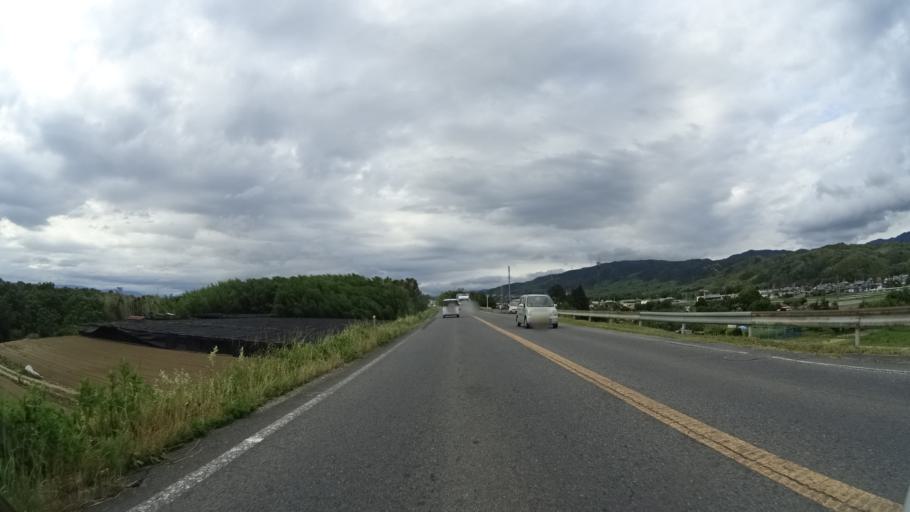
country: JP
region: Kyoto
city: Tanabe
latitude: 34.7775
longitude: 135.8062
